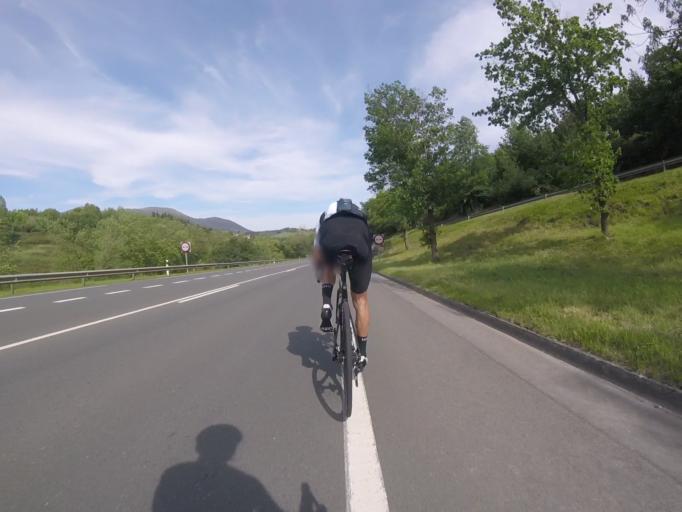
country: ES
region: Basque Country
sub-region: Provincia de Guipuzcoa
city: Cestona
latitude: 43.2578
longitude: -2.2696
